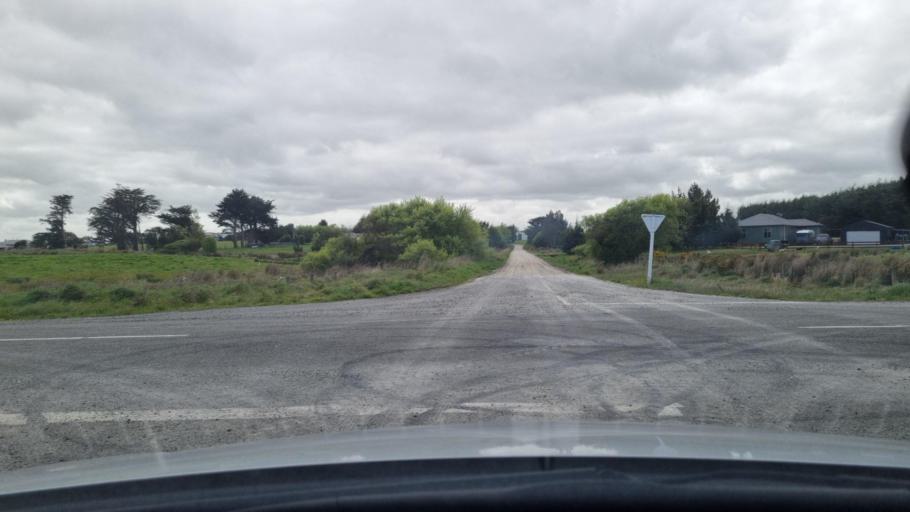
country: NZ
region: Southland
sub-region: Invercargill City
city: Invercargill
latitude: -46.4359
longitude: 168.3896
